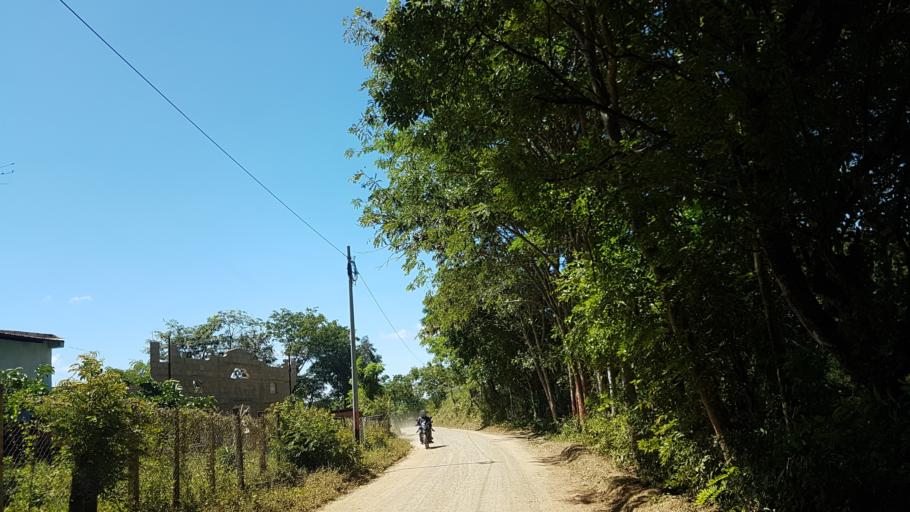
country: HN
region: El Paraiso
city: Santa Cruz
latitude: 13.7352
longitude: -86.6740
